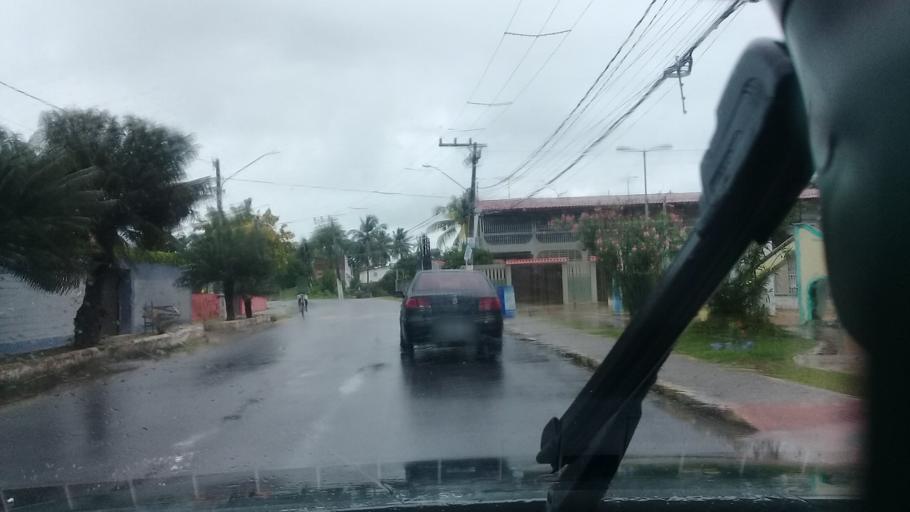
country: BR
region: Pernambuco
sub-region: Itamaraca
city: Itamaraca
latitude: -7.7358
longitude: -34.8258
